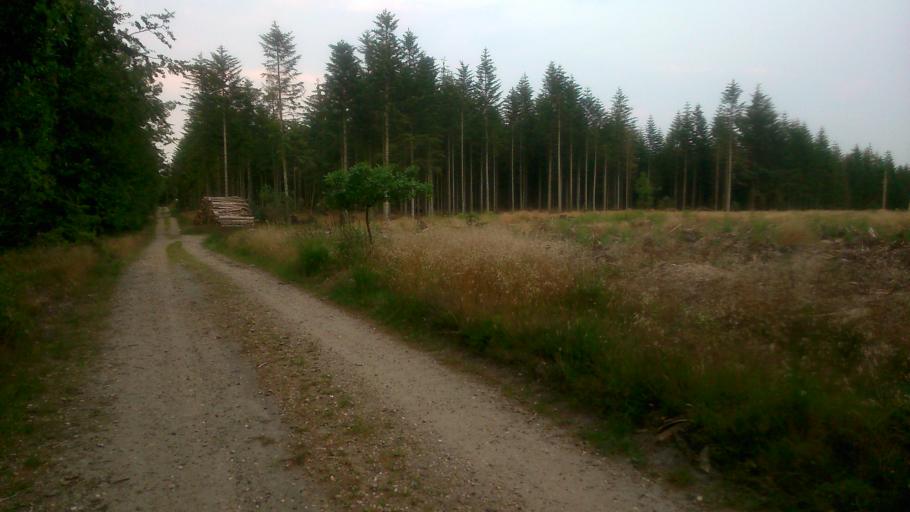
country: DK
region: Central Jutland
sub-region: Ringkobing-Skjern Kommune
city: Skjern
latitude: 56.0045
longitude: 8.4562
